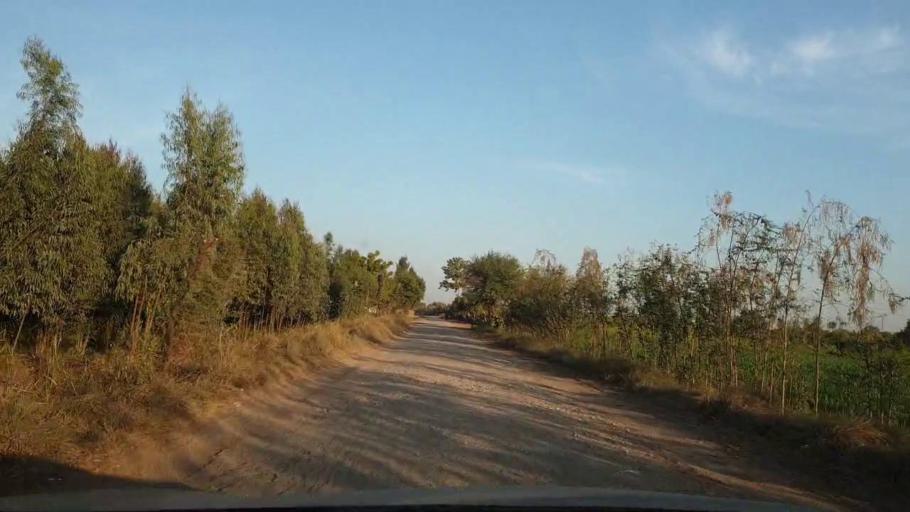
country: PK
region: Sindh
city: Tando Adam
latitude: 25.6169
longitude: 68.6744
